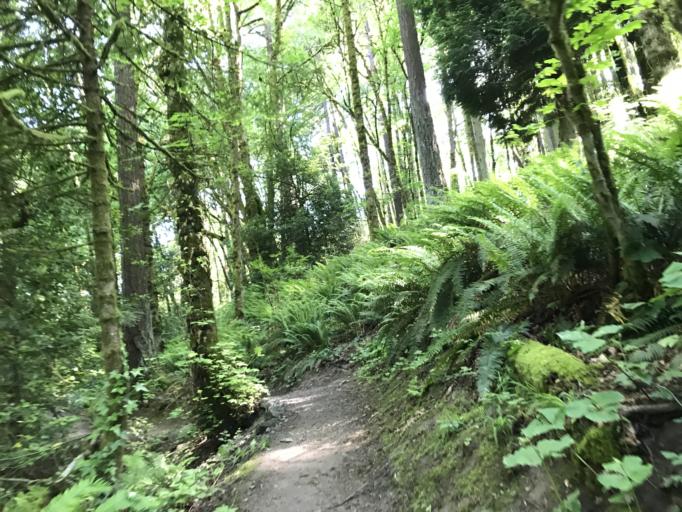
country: US
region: Oregon
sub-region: Multnomah County
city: Portland
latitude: 45.4945
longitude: -122.6894
